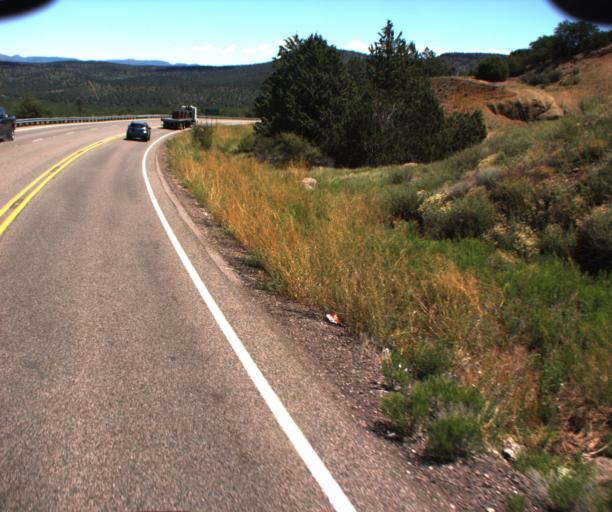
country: US
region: Arizona
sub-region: Navajo County
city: Cibecue
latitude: 33.7443
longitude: -110.5285
